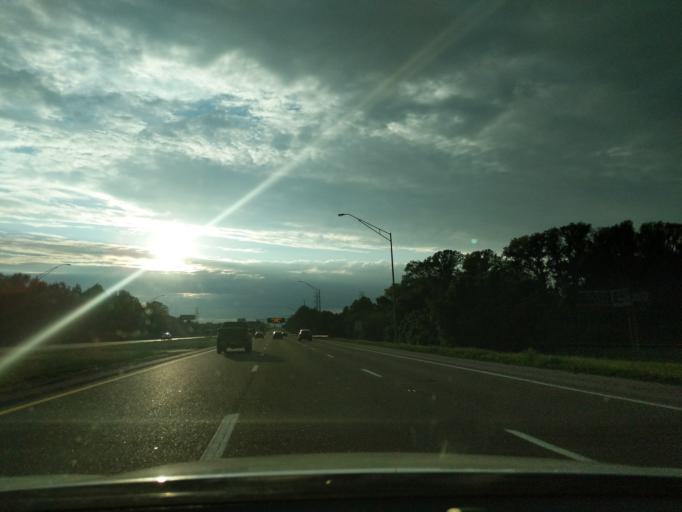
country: US
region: Tennessee
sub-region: Shelby County
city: New South Memphis
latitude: 35.0748
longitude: -90.0364
